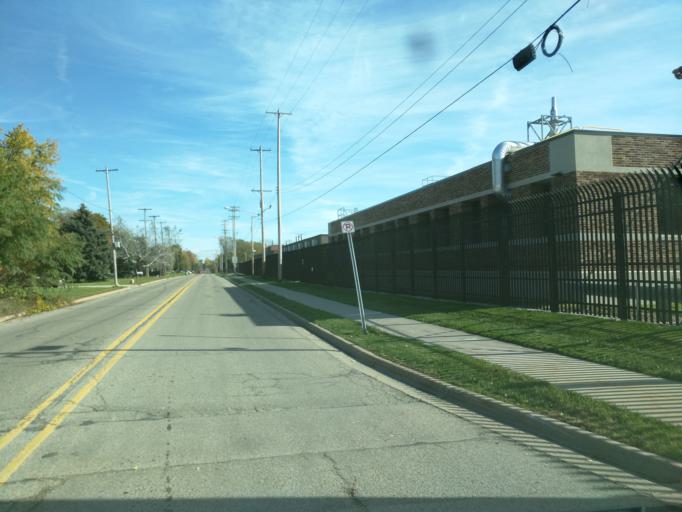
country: US
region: Michigan
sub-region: Ingham County
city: Edgemont Park
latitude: 42.7697
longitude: -84.5671
